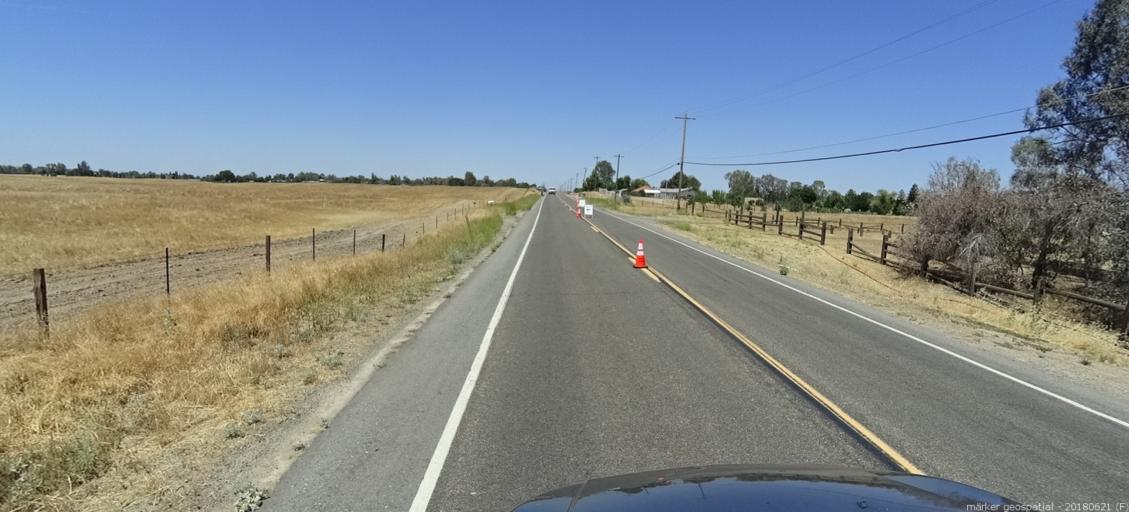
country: US
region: California
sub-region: Madera County
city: Bonadelle Ranchos-Madera Ranchos
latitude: 36.9666
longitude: -119.8860
